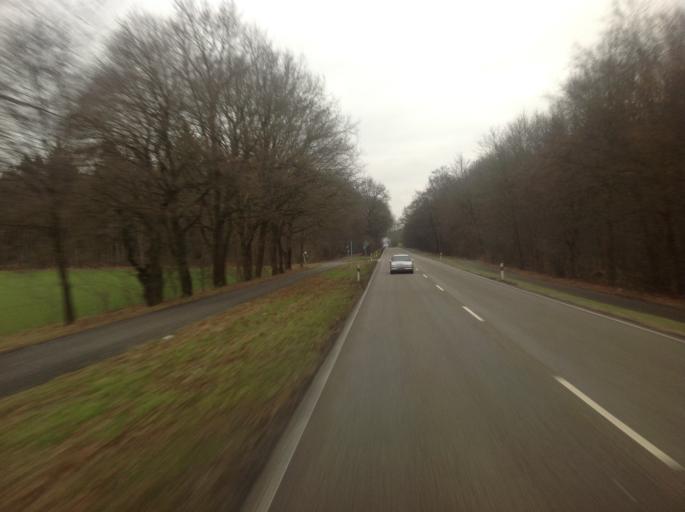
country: DE
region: Baden-Wuerttemberg
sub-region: Karlsruhe Region
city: Hugelsheim
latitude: 48.8050
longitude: 8.1297
